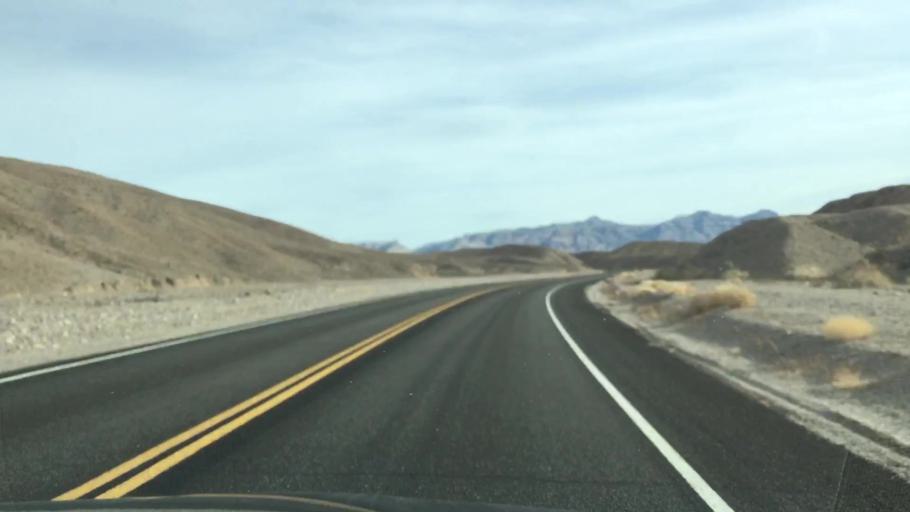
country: US
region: Nevada
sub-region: Nye County
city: Beatty
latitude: 36.6553
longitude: -117.0253
